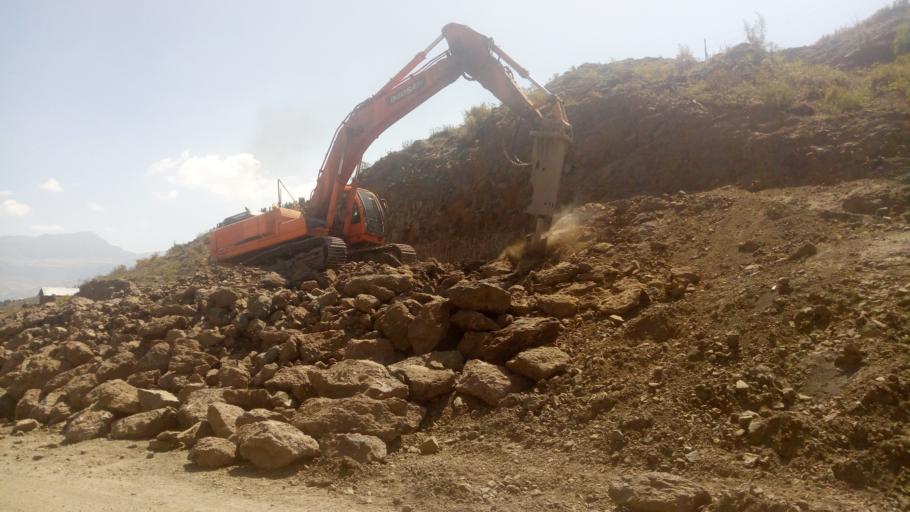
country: ET
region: Tigray
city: Maych'ew
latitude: 12.9658
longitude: 39.4639
